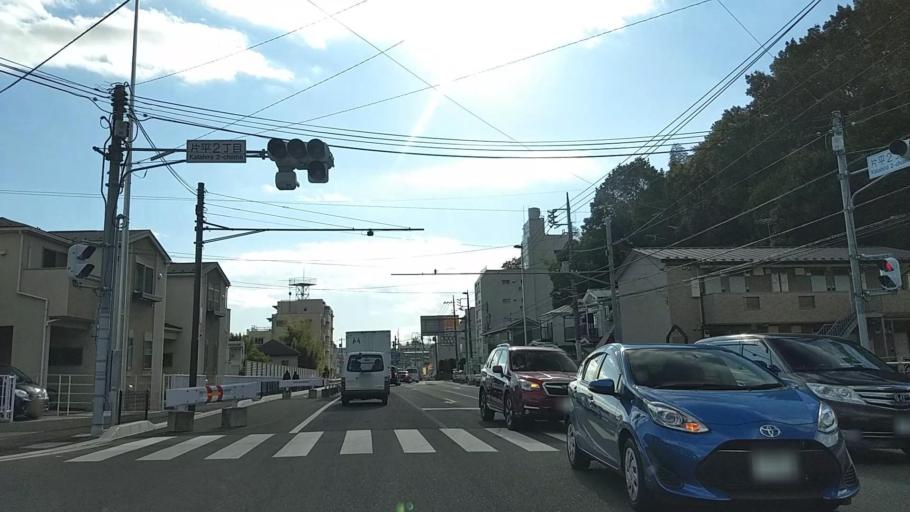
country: JP
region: Tokyo
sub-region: Machida-shi
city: Machida
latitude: 35.5933
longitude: 139.4982
